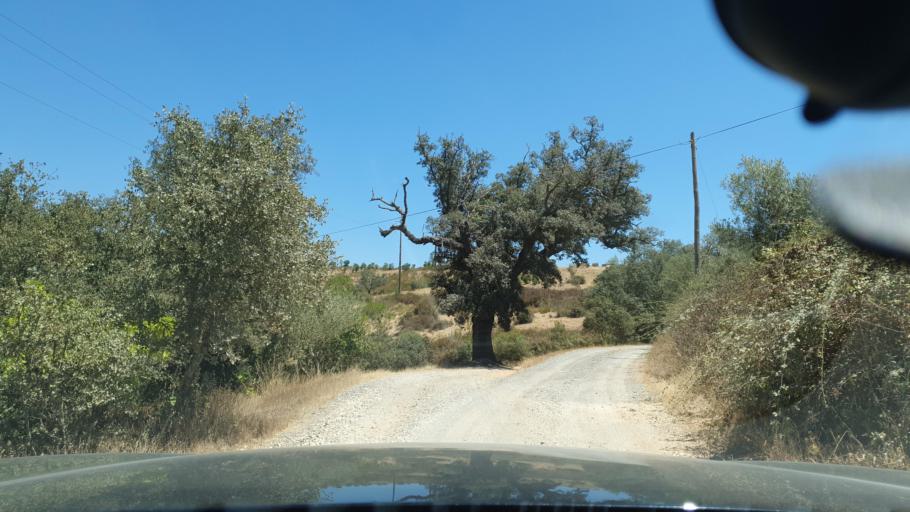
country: PT
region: Beja
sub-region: Odemira
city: Odemira
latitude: 37.5139
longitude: -8.4733
